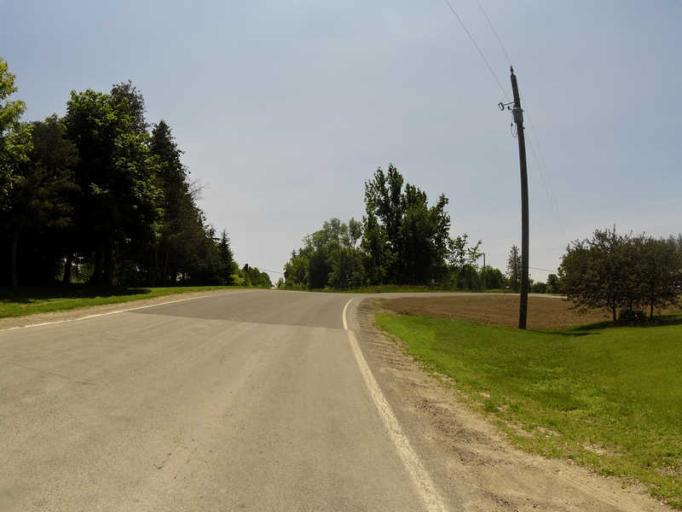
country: CA
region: Ontario
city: Peterborough
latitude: 44.3869
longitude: -78.2690
